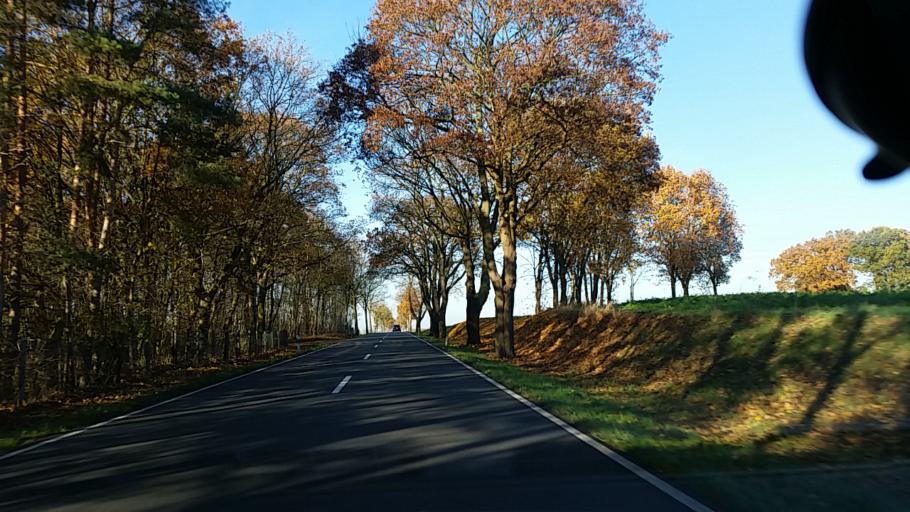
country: DE
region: Saxony-Anhalt
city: Jubar
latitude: 52.6843
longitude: 10.8261
